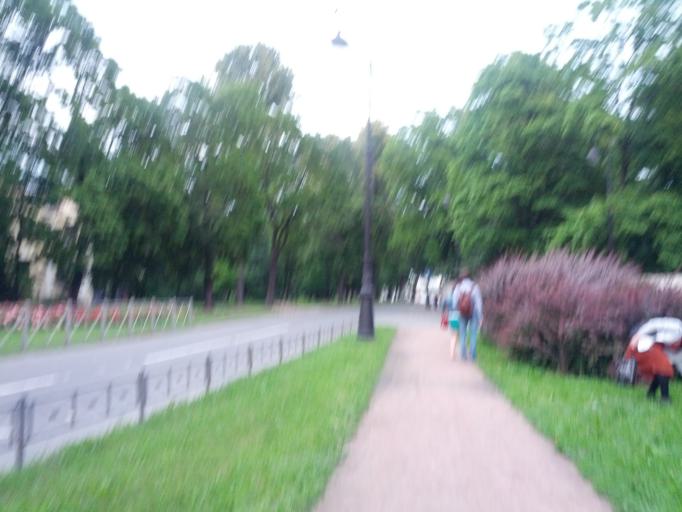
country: RU
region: St.-Petersburg
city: Novaya Derevnya
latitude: 59.9766
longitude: 30.2931
